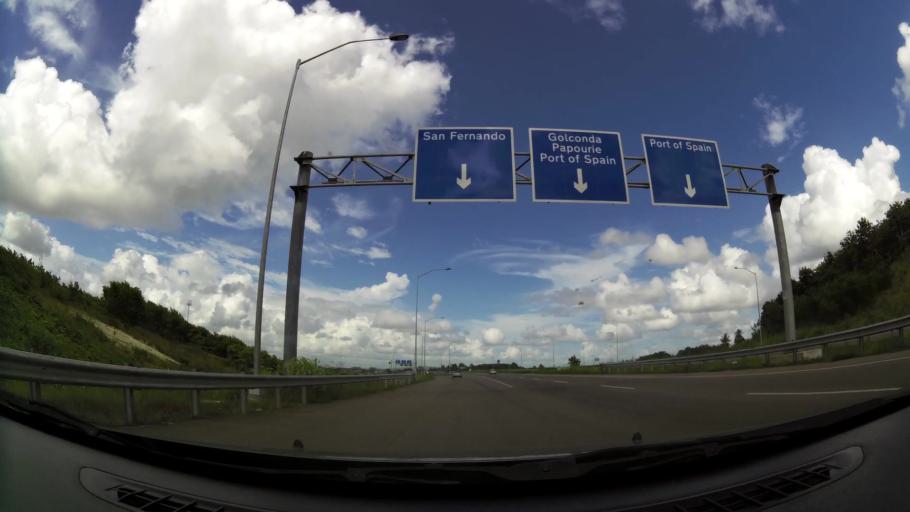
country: TT
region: City of San Fernando
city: Mon Repos
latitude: 10.2500
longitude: -61.4417
